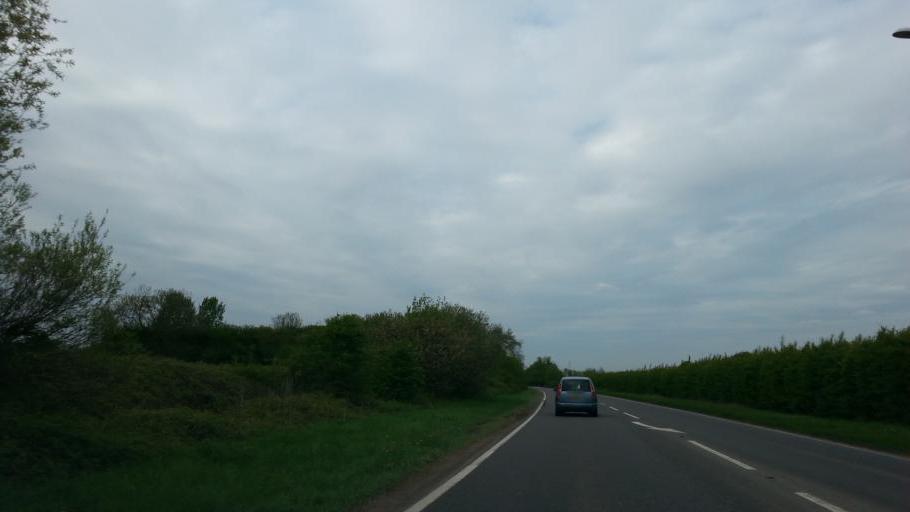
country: GB
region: England
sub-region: Cambridgeshire
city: Doddington
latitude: 52.5136
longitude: 0.0895
